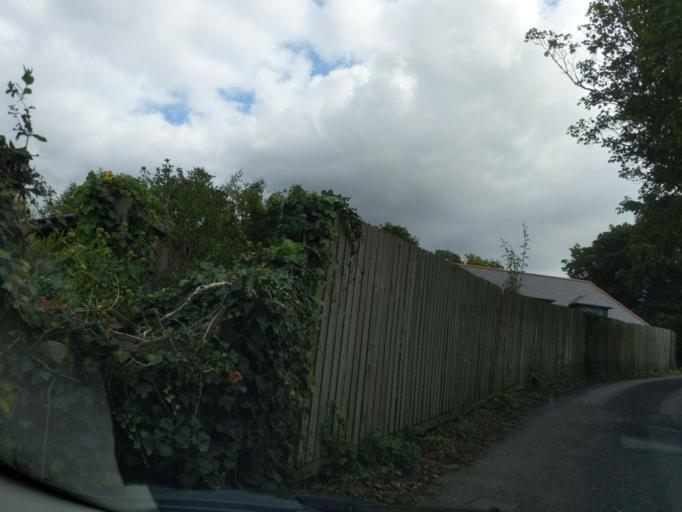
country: GB
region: England
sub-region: Plymouth
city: Plymstock
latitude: 50.3502
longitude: -4.1089
